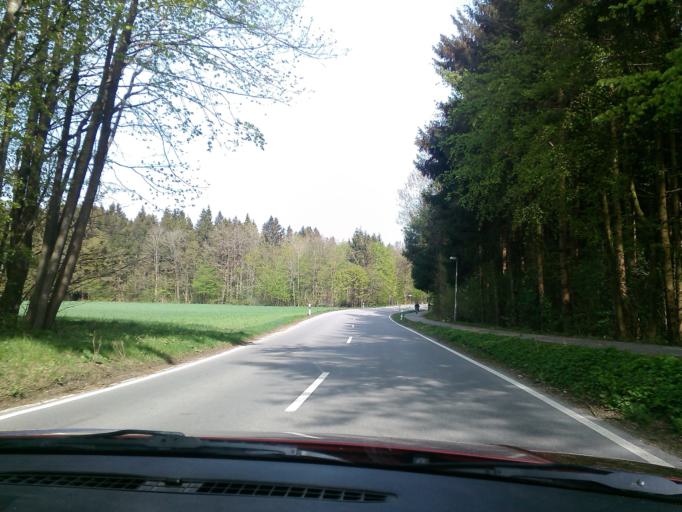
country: DE
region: Bavaria
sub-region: Upper Bavaria
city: Gauting
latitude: 48.0692
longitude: 11.3444
